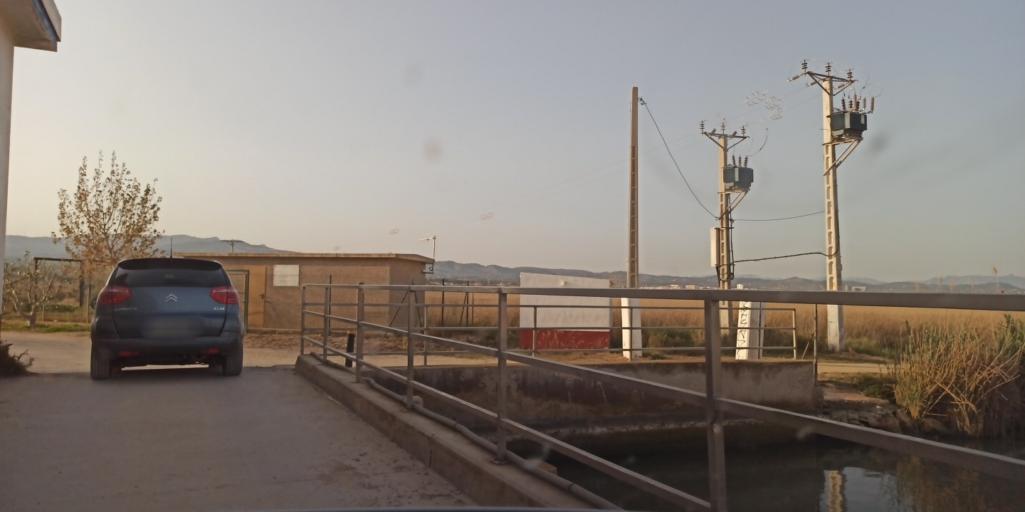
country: ES
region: Catalonia
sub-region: Provincia de Tarragona
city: L'Ampolla
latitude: 40.7851
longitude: 0.7027
